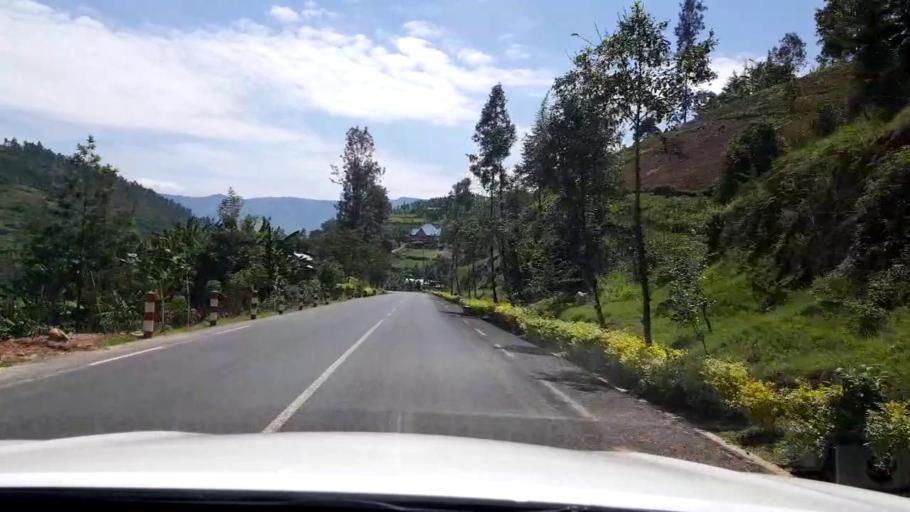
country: RW
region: Southern Province
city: Gitarama
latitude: -1.9195
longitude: 29.6421
